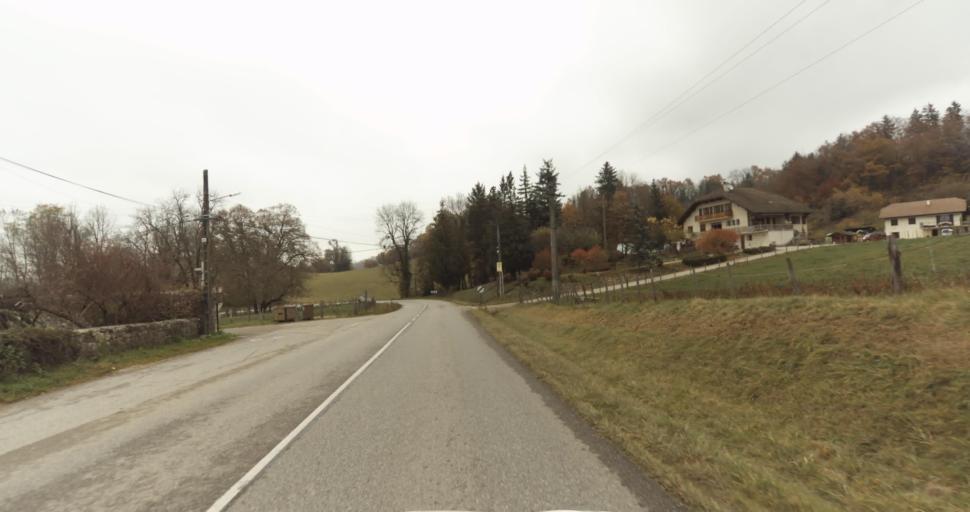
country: FR
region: Rhone-Alpes
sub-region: Departement de la Haute-Savoie
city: Viuz-la-Chiesaz
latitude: 45.8278
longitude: 6.0606
